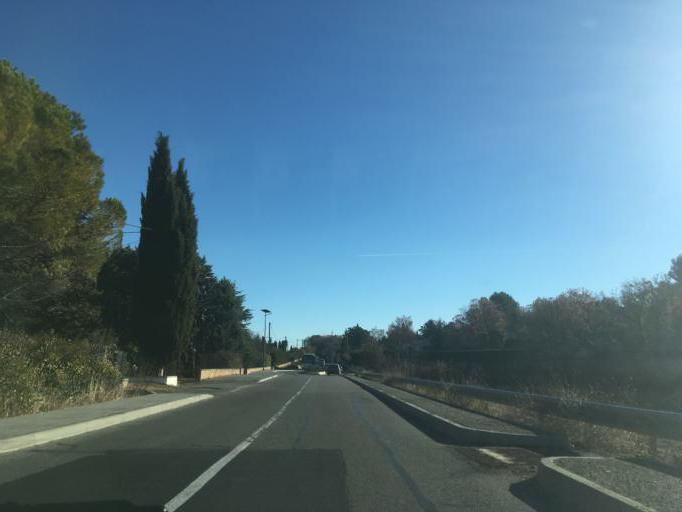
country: FR
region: Provence-Alpes-Cote d'Azur
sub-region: Departement du Var
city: Flayosc
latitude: 43.5396
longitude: 6.3791
